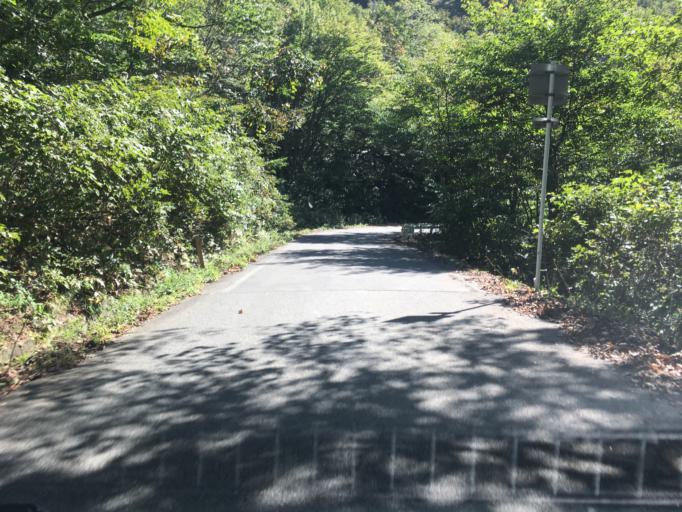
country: JP
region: Yamagata
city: Yonezawa
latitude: 37.8011
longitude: 140.2724
